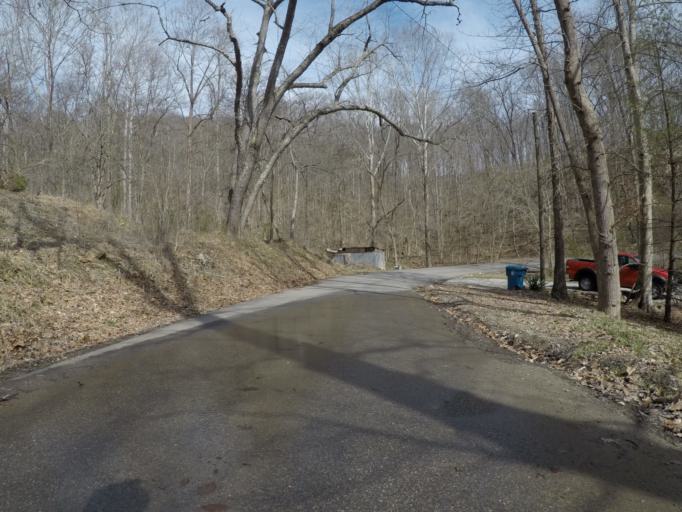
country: US
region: West Virginia
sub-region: Wayne County
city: Ceredo
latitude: 38.3744
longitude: -82.5423
